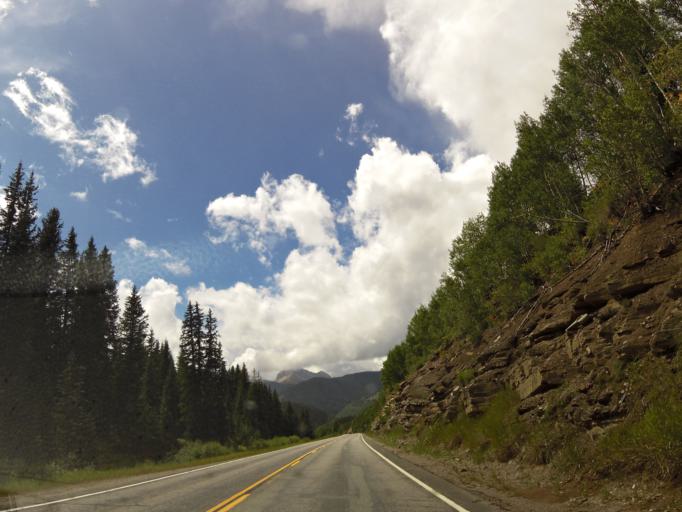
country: US
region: Colorado
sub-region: San Juan County
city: Silverton
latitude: 37.7306
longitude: -107.7247
